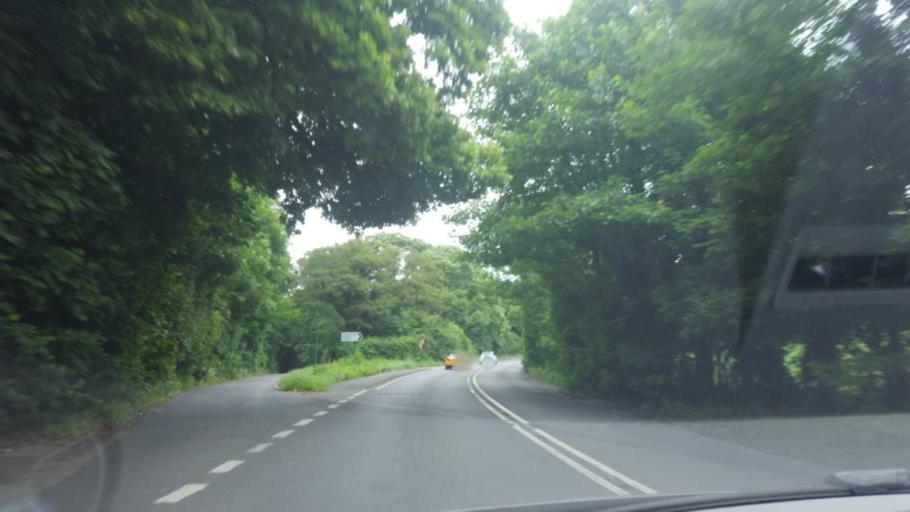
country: GB
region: England
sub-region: Royal Borough of Windsor and Maidenhead
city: Hurley
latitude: 51.5414
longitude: -0.8051
